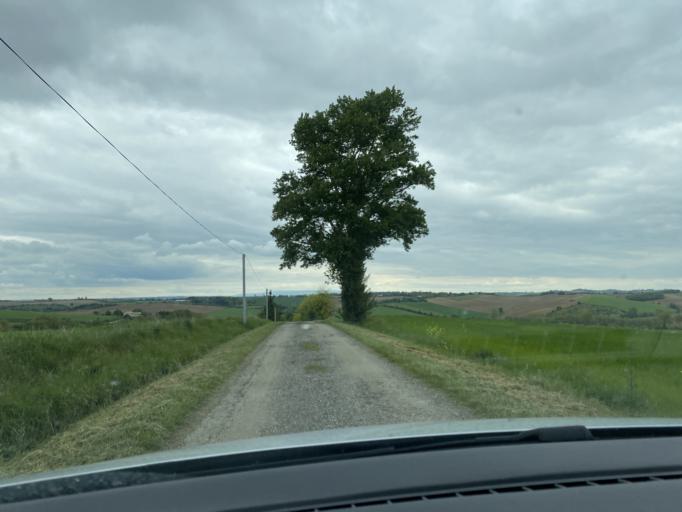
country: FR
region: Midi-Pyrenees
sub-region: Departement de la Haute-Garonne
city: Nailloux
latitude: 43.3640
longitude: 1.6387
